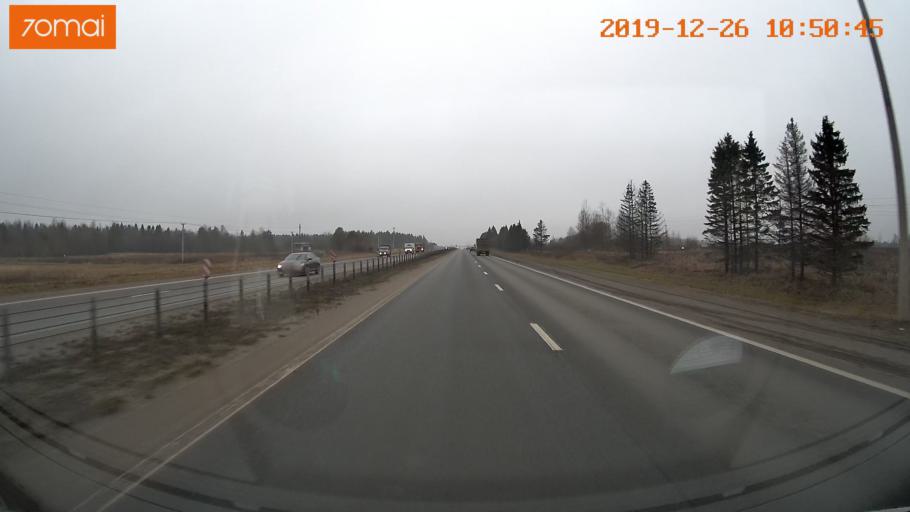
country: RU
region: Vologda
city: Molochnoye
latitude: 59.2072
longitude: 39.6802
